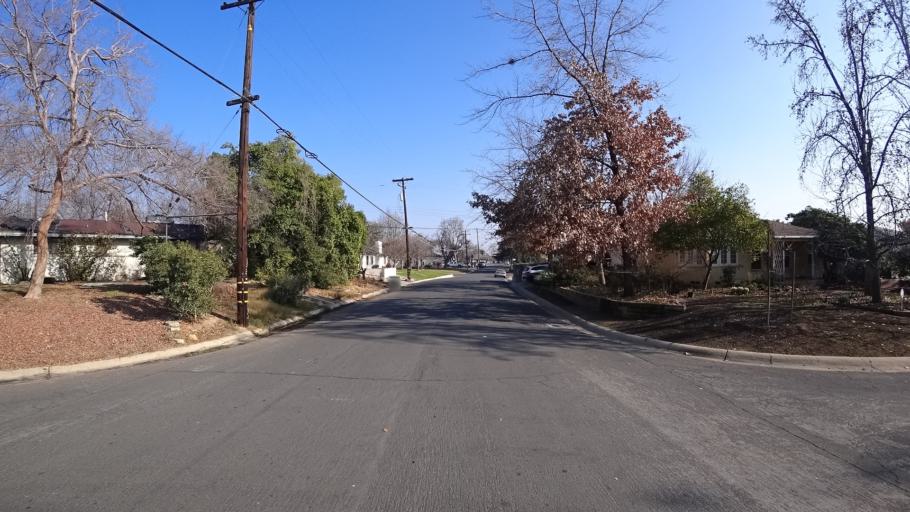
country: US
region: California
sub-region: Kern County
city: Bakersfield
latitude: 35.3952
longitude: -118.9962
